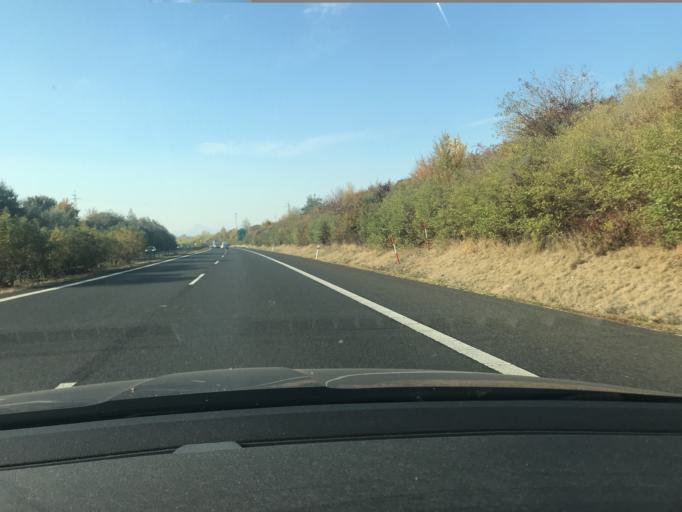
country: CZ
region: Ustecky
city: Roudnice nad Labem
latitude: 50.4324
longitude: 14.1915
